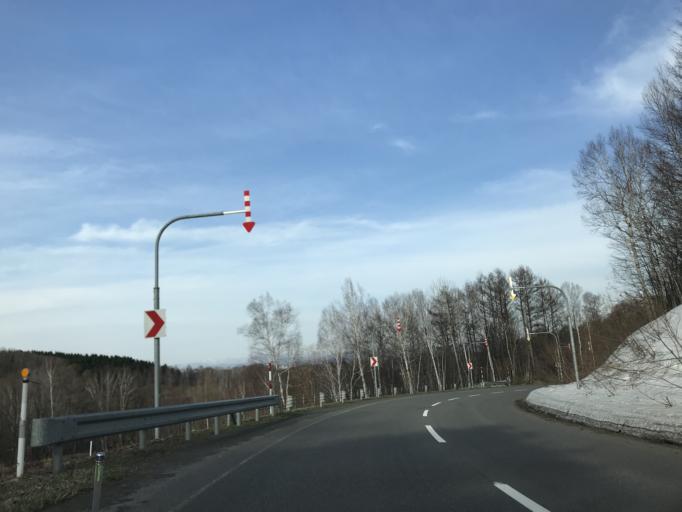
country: JP
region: Hokkaido
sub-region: Asahikawa-shi
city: Asahikawa
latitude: 43.6975
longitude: 142.3281
